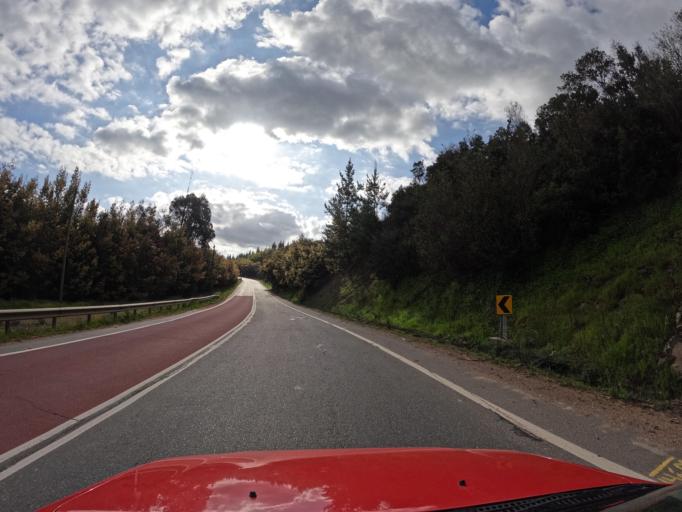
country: CL
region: Maule
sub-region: Provincia de Talca
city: Constitucion
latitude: -35.5514
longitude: -72.1426
